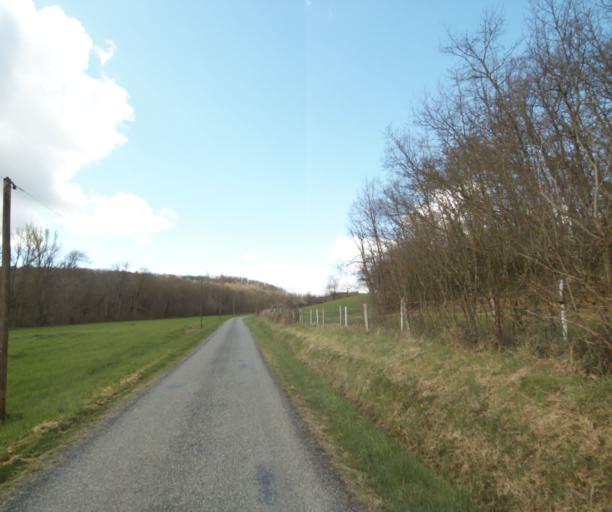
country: FR
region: Midi-Pyrenees
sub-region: Departement de l'Ariege
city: Saverdun
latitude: 43.1857
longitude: 1.5581
